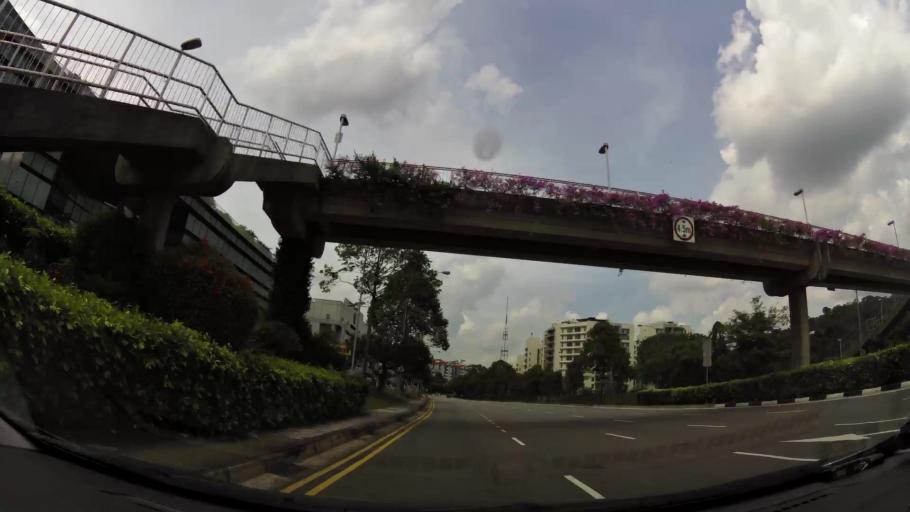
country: SG
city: Singapore
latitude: 1.3447
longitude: 103.7747
